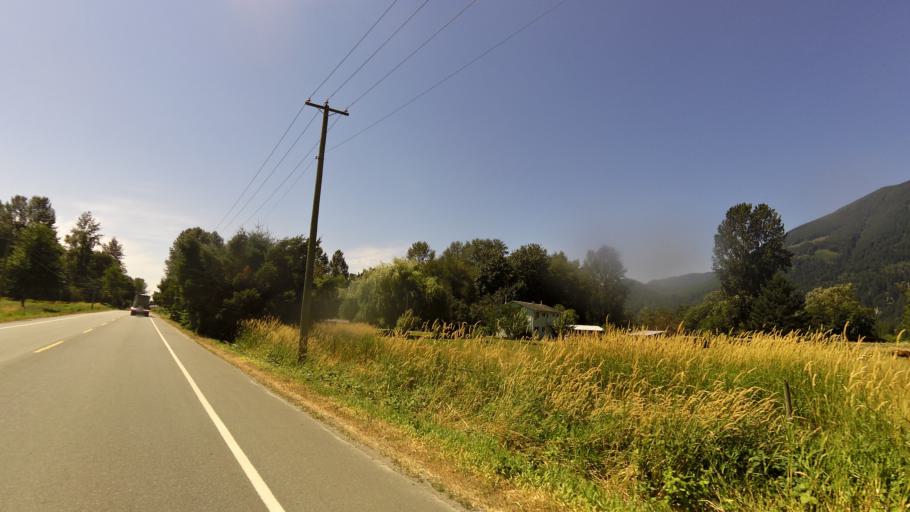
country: CA
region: British Columbia
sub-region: Fraser Valley Regional District
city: Chilliwack
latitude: 49.1717
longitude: -122.0883
